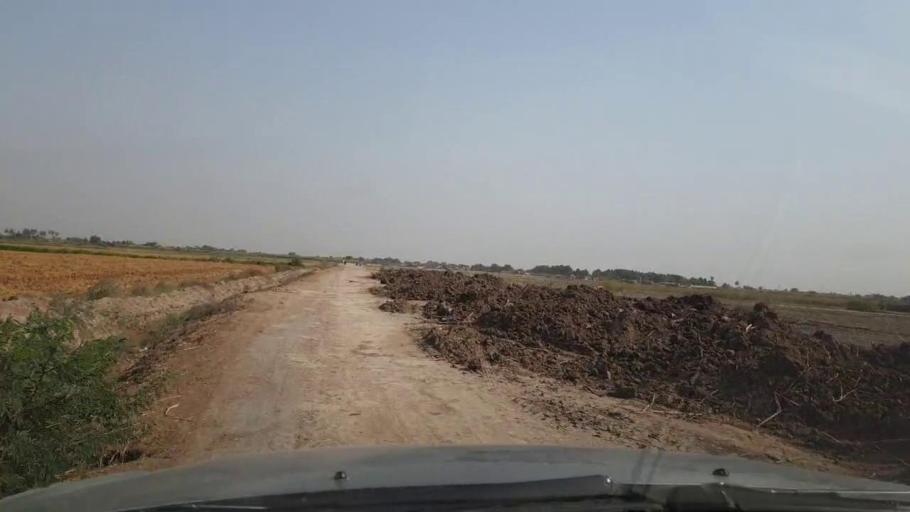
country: PK
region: Sindh
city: Bulri
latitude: 24.9158
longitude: 68.3603
